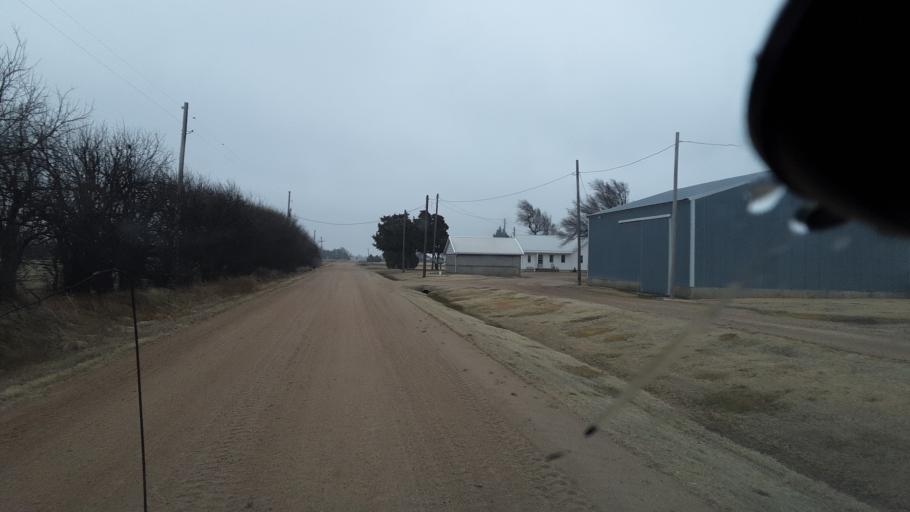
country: US
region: Kansas
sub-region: Reno County
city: South Hutchinson
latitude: 37.9845
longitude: -97.9987
